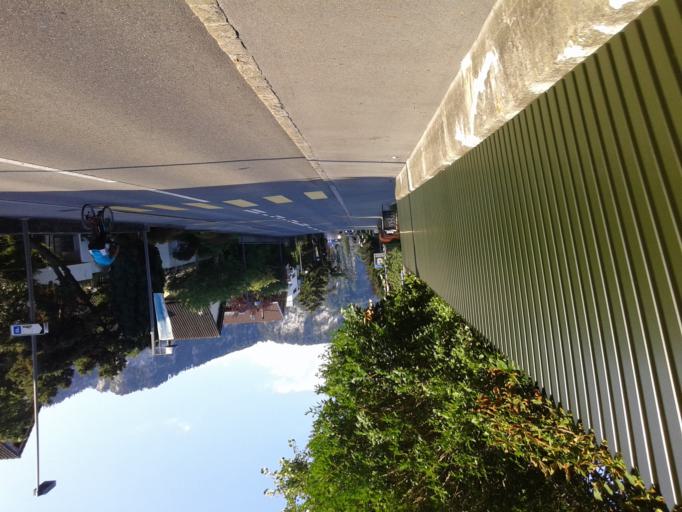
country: CH
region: Nidwalden
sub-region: Nidwalden
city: Hergiswil
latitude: 46.9957
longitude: 8.3128
